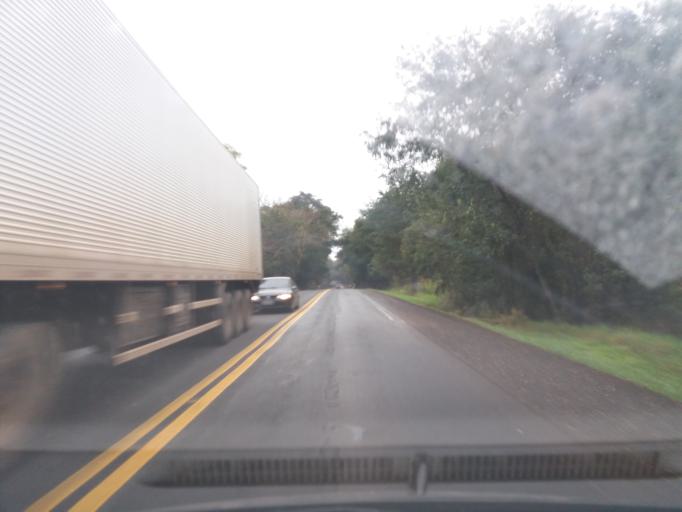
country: BR
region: Parana
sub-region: Ampere
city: Ampere
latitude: -25.8494
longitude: -53.5026
